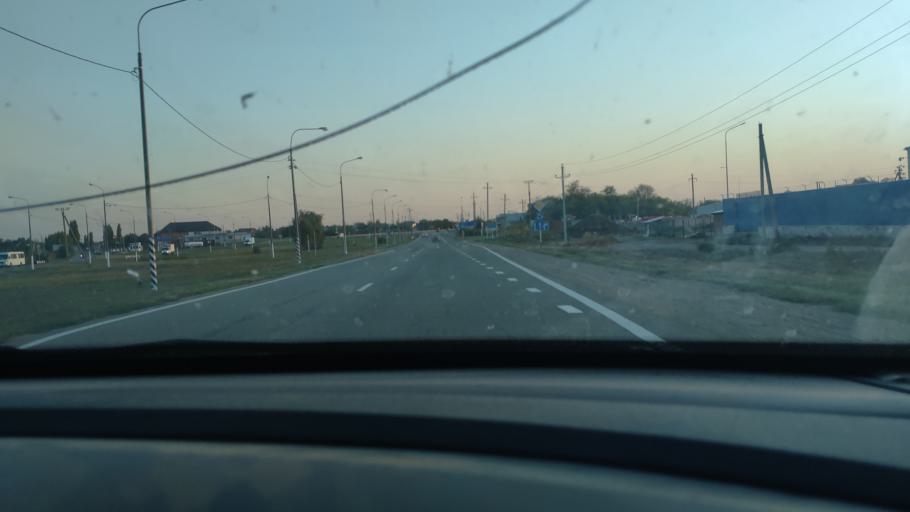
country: RU
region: Krasnodarskiy
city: Timashevsk
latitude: 45.6110
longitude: 38.9870
